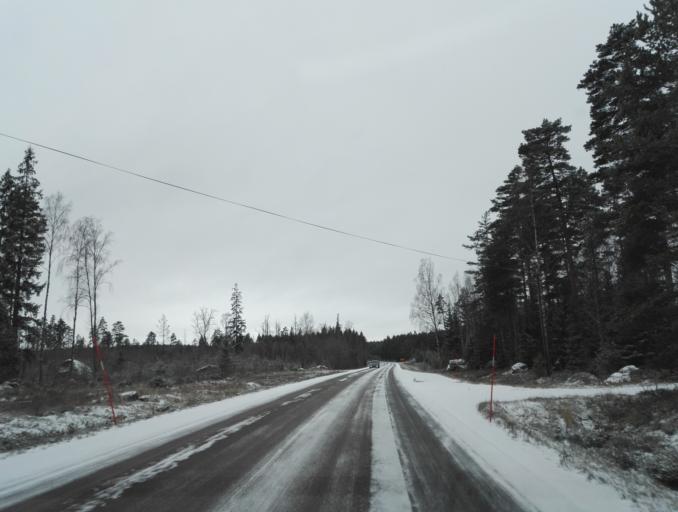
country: SE
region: Kronoberg
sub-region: Lessebo Kommun
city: Lessebo
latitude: 56.6864
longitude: 15.1806
